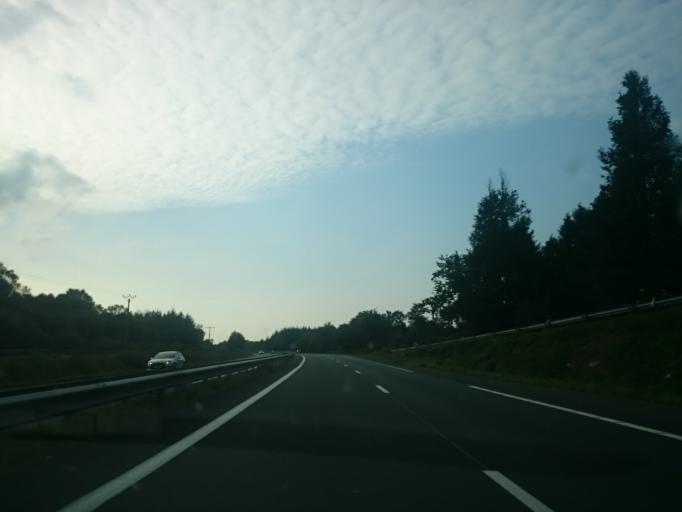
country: FR
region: Brittany
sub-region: Departement du Finistere
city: Guerlesquin
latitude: 48.5667
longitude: -3.5494
